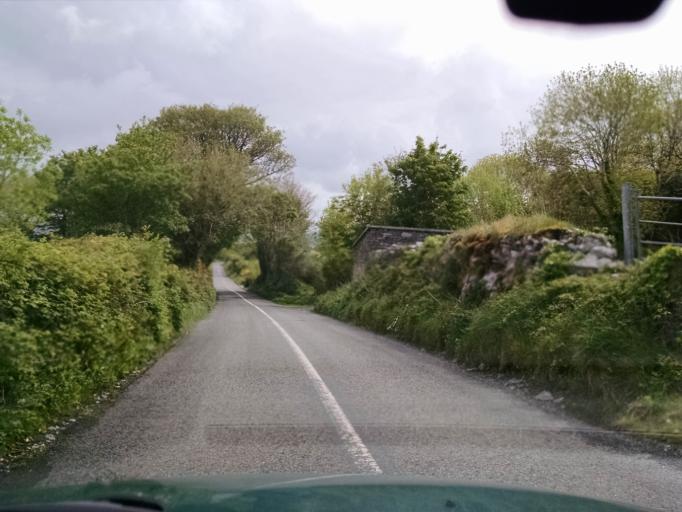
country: IE
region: Connaught
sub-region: County Galway
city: Bearna
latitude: 53.1342
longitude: -9.2075
